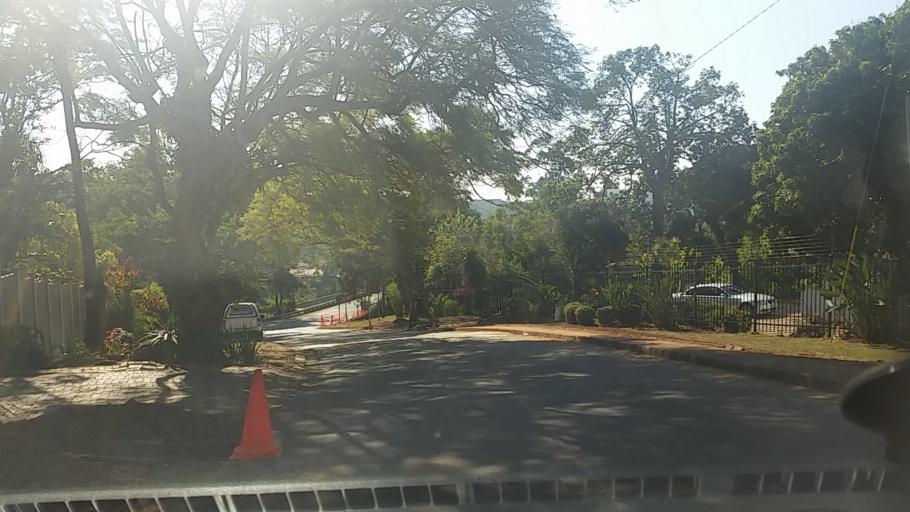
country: ZA
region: KwaZulu-Natal
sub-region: eThekwini Metropolitan Municipality
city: Berea
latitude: -29.8418
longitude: 30.9143
